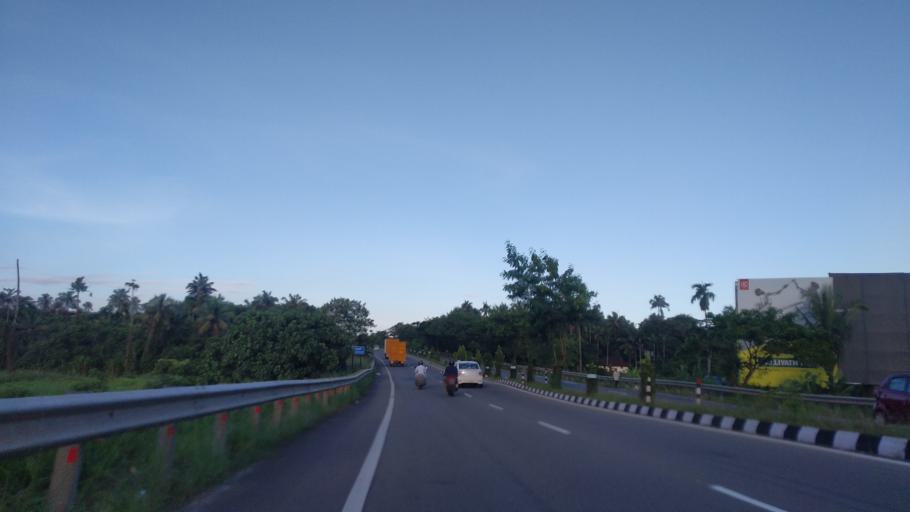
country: IN
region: Kerala
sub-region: Ernakulam
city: Elur
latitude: 10.0649
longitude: 76.2959
